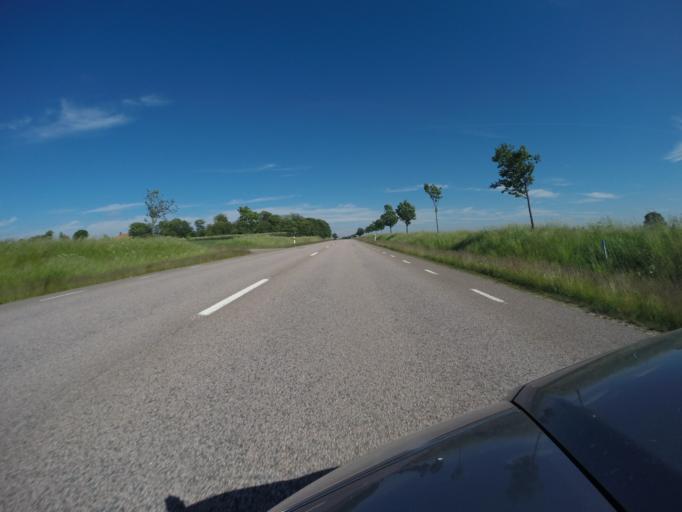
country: SE
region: Skane
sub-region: Bjuvs Kommun
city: Bjuv
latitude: 56.0122
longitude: 12.9330
